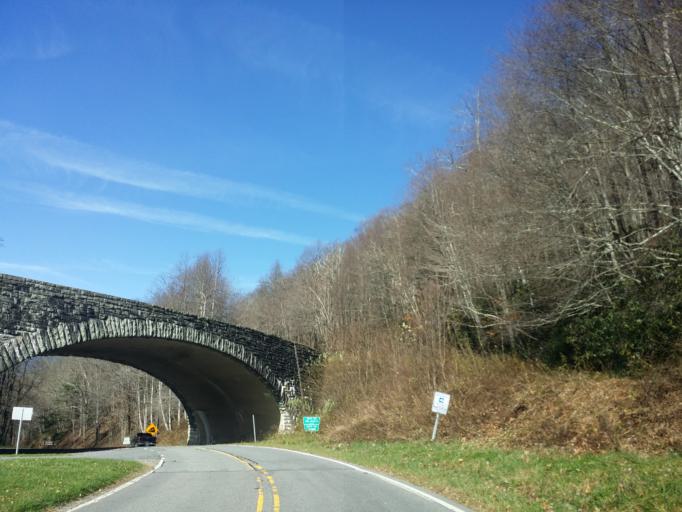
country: US
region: North Carolina
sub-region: Mitchell County
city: Spruce Pine
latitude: 35.7706
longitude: -82.1645
